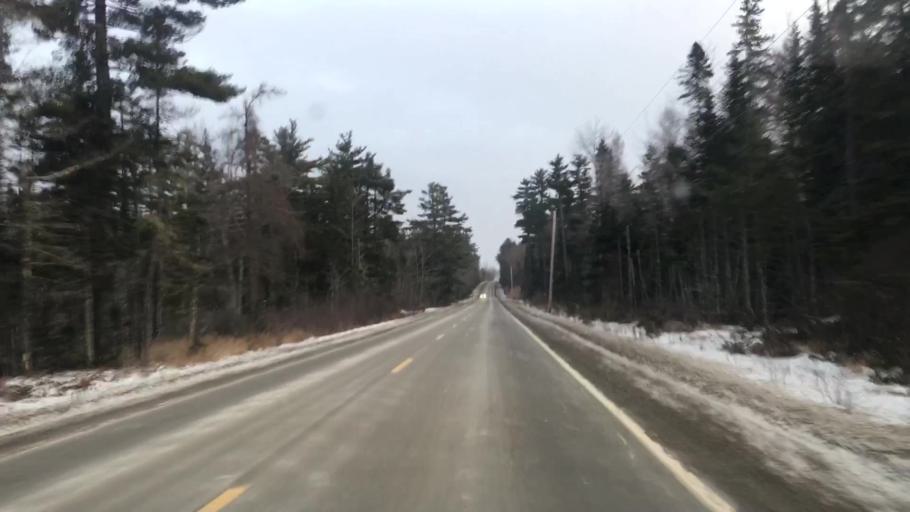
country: US
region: Maine
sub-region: Hancock County
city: Ellsworth
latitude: 44.6773
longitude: -68.3529
